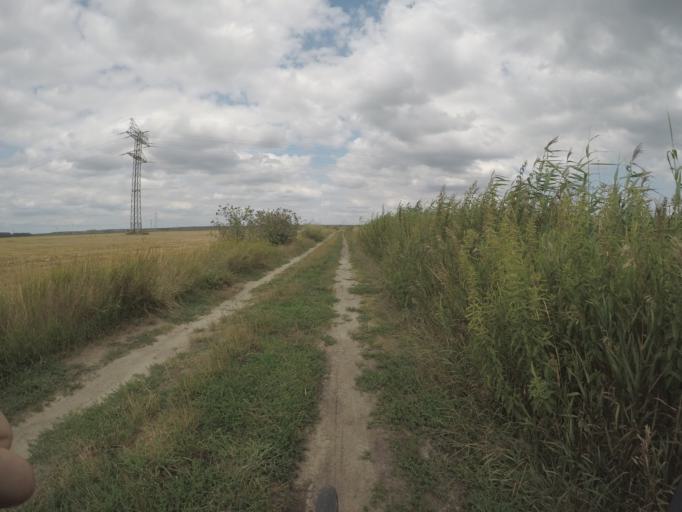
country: DE
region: Brandenburg
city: Falkensee
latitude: 52.6078
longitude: 13.0615
